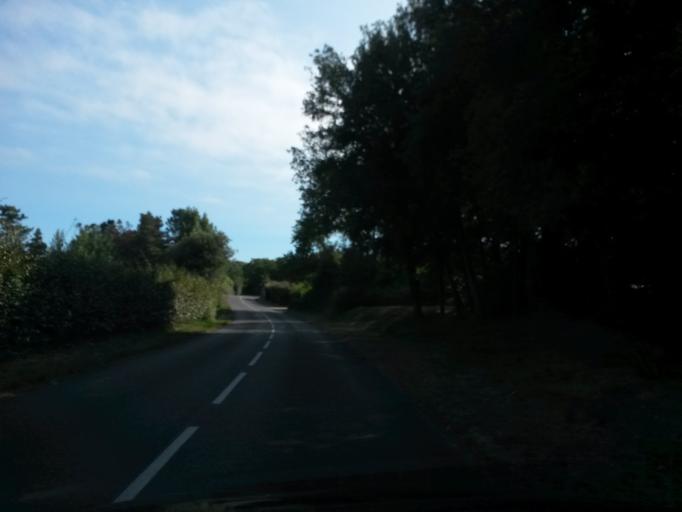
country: FR
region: Pays de la Loire
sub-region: Departement de la Vendee
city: Les Sables-d'Olonne
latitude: 46.5265
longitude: -1.8107
